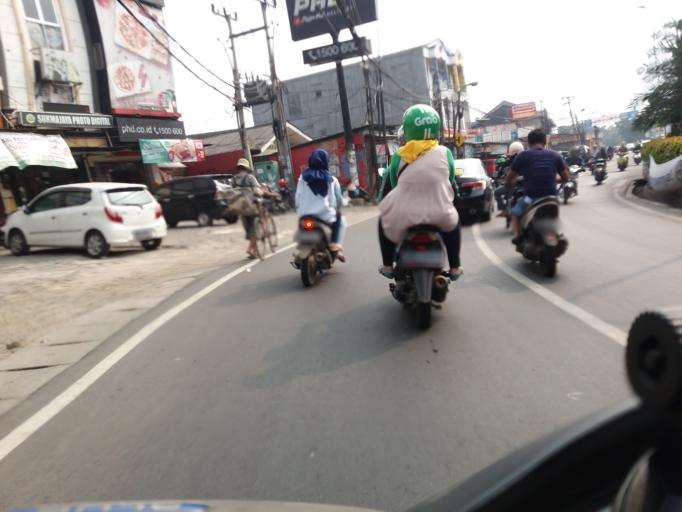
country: ID
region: West Java
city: Depok
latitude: -6.4045
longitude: 106.8415
